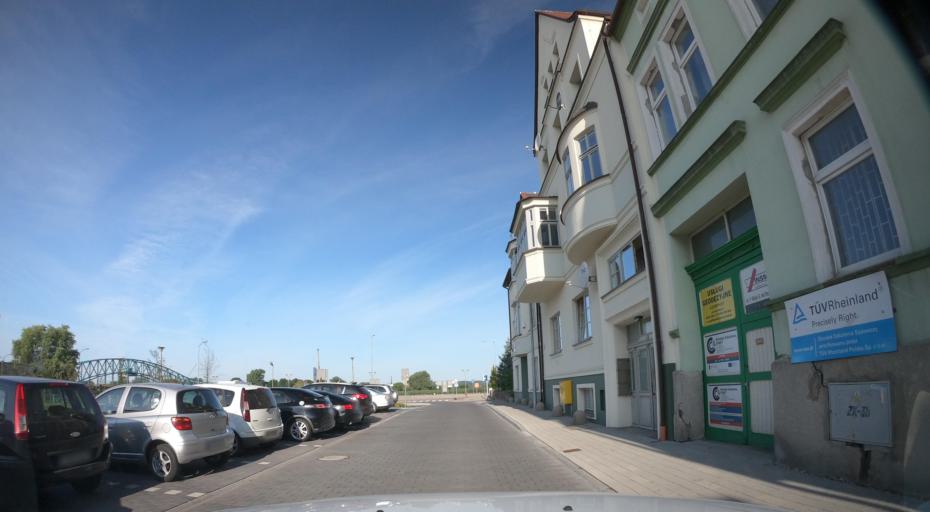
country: PL
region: West Pomeranian Voivodeship
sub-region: Powiat gryfinski
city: Gryfino
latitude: 53.2545
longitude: 14.4849
